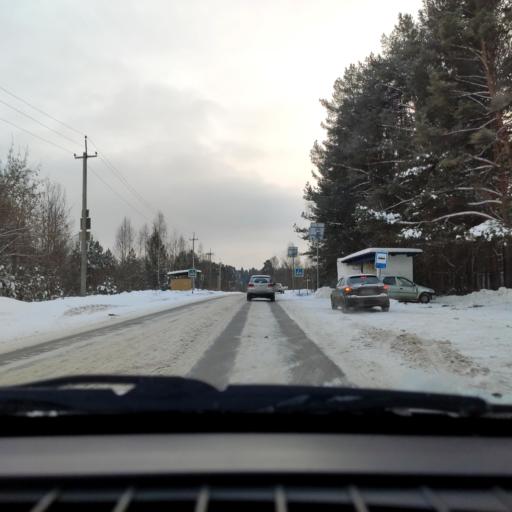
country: RU
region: Perm
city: Overyata
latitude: 58.0490
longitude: 55.8851
